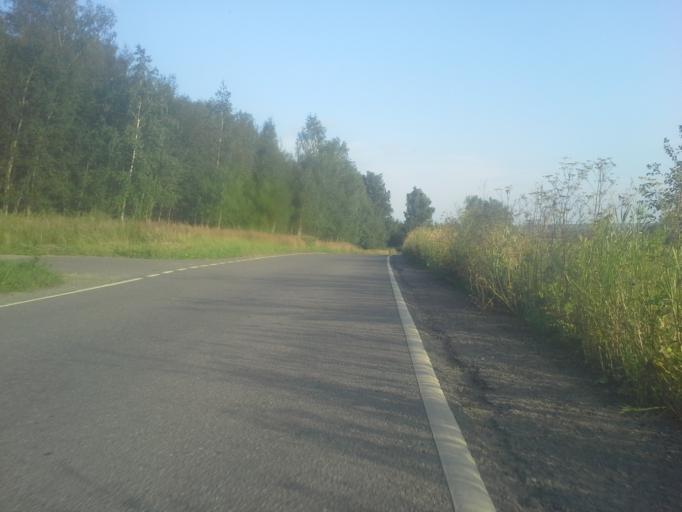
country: RU
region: Moskovskaya
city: Nikolina Gora
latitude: 55.7475
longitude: 36.9822
